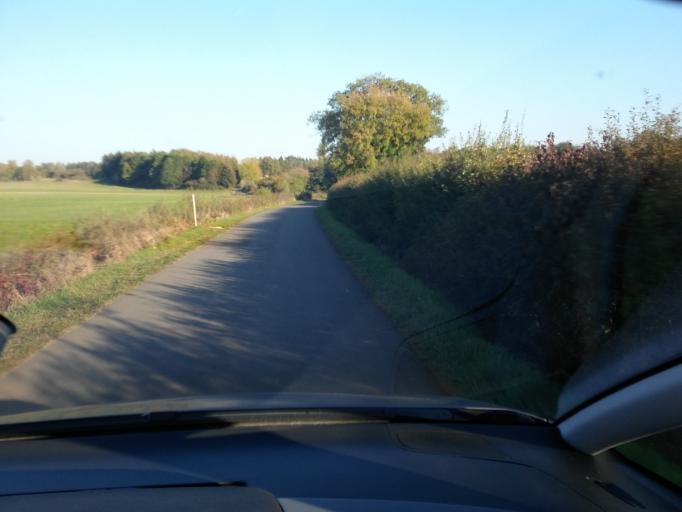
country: LU
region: Luxembourg
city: Eischen
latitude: 49.6852
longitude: 5.8513
